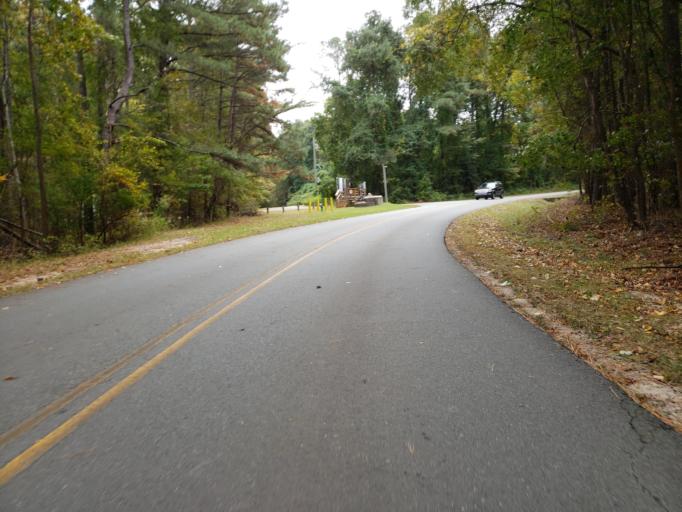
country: US
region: North Carolina
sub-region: Chatham County
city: Fearrington Village
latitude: 35.7471
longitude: -79.0367
